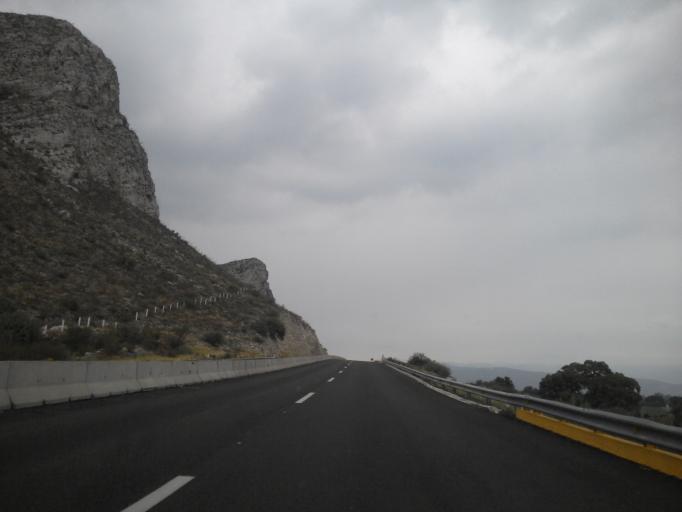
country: MX
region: Durango
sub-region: Lerdo
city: La Goma
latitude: 25.4790
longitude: -103.6479
